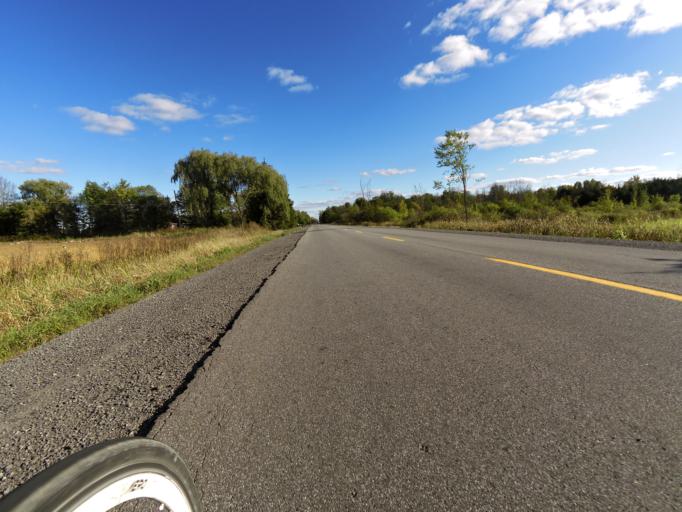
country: CA
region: Ontario
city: Bells Corners
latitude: 45.1590
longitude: -75.7833
